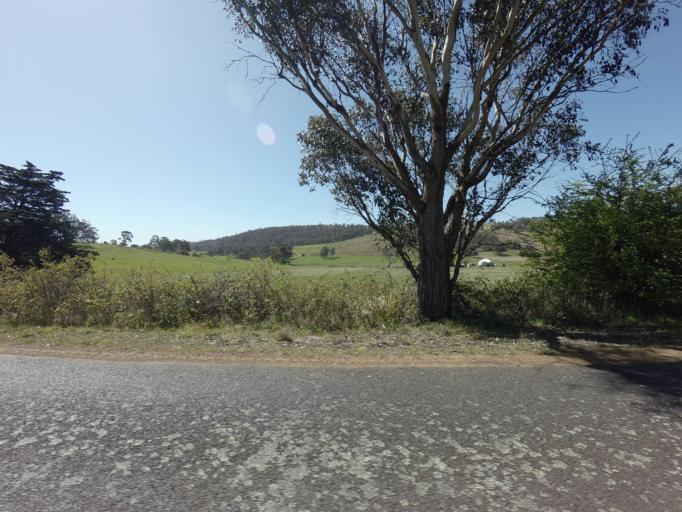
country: AU
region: Tasmania
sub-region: Derwent Valley
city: New Norfolk
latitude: -42.6327
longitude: 146.7364
